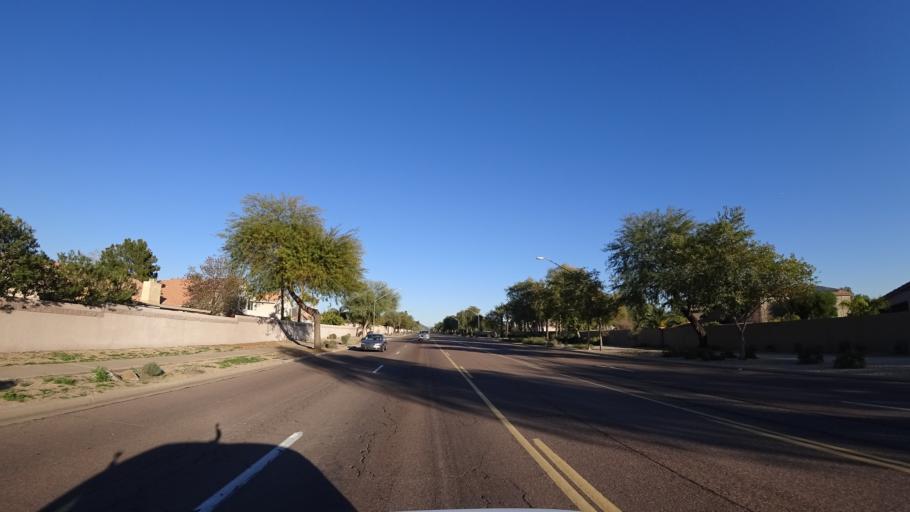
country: US
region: Arizona
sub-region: Maricopa County
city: Sun City
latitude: 33.6818
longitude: -112.2175
